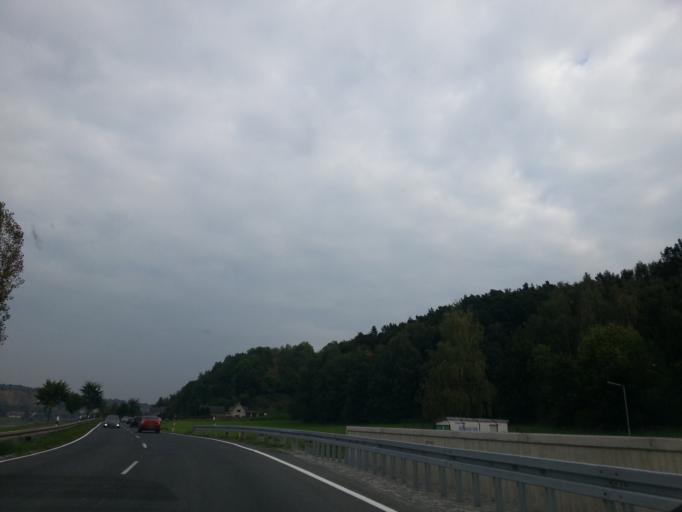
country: DE
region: Saxony
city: Meissen
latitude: 51.1892
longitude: 13.4258
